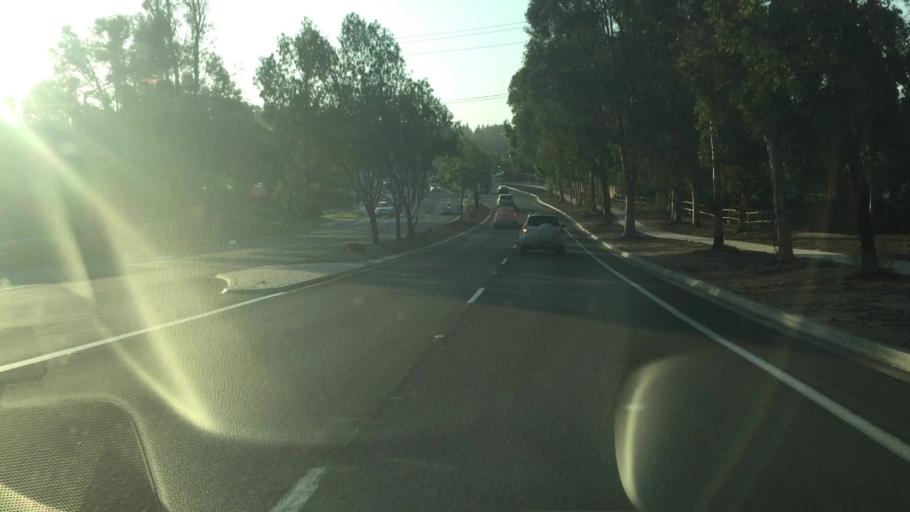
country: US
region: California
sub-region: San Diego County
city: Poway
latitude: 32.9820
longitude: -117.0602
